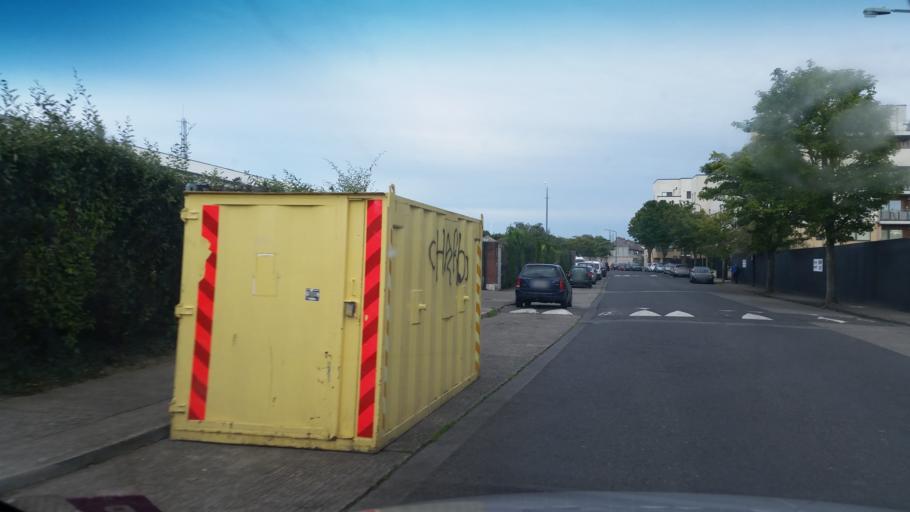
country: IE
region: Leinster
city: Beaumont
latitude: 53.3889
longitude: -6.2536
